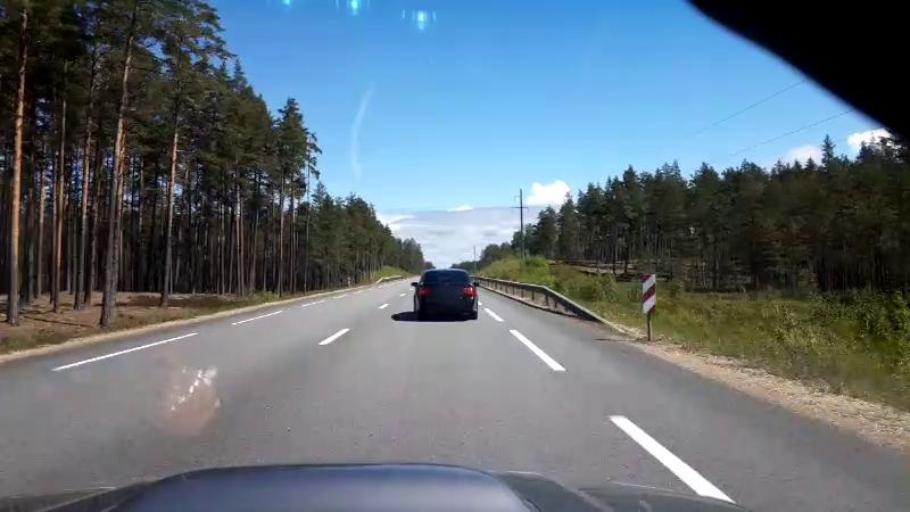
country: LV
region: Saulkrastu
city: Saulkrasti
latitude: 57.2112
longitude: 24.3926
